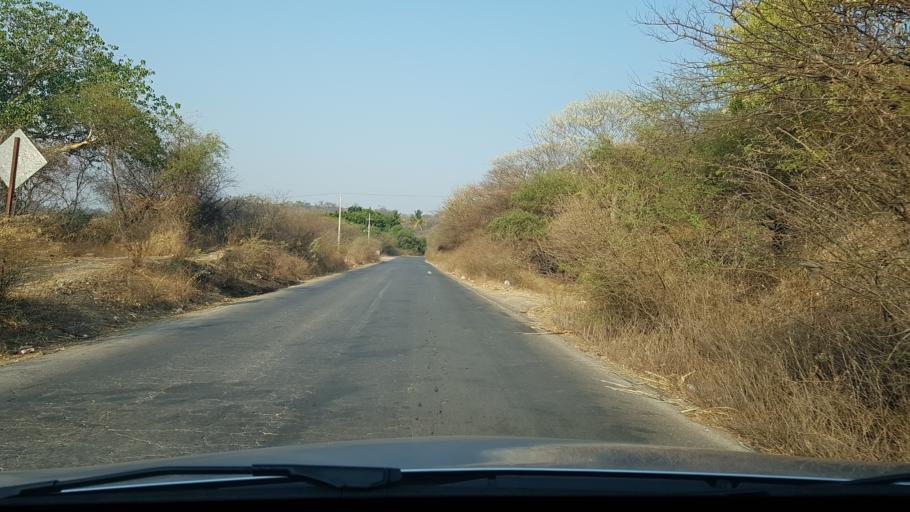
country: MX
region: Morelos
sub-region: Tepalcingo
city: Zacapalco
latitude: 18.6372
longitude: -99.0140
